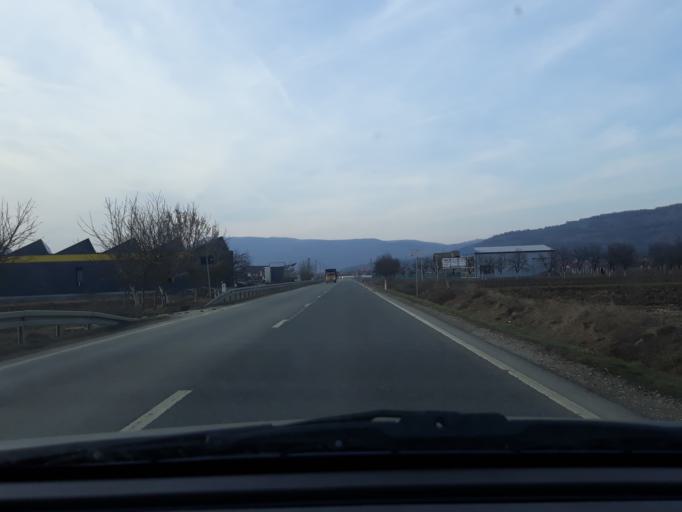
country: RO
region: Salaj
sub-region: Comuna Periceiu
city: Periceiu
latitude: 47.2225
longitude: 22.8807
